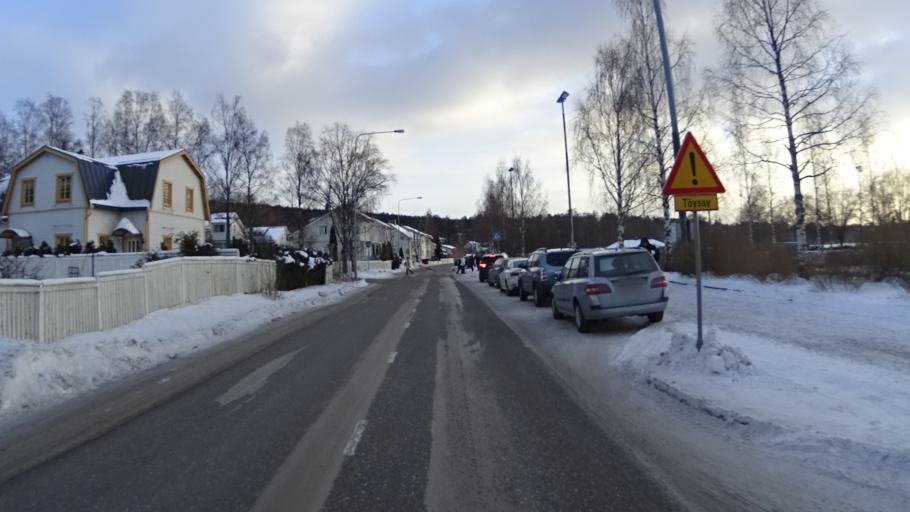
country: FI
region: Uusimaa
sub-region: Helsinki
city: Lohja
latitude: 60.2503
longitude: 24.0553
